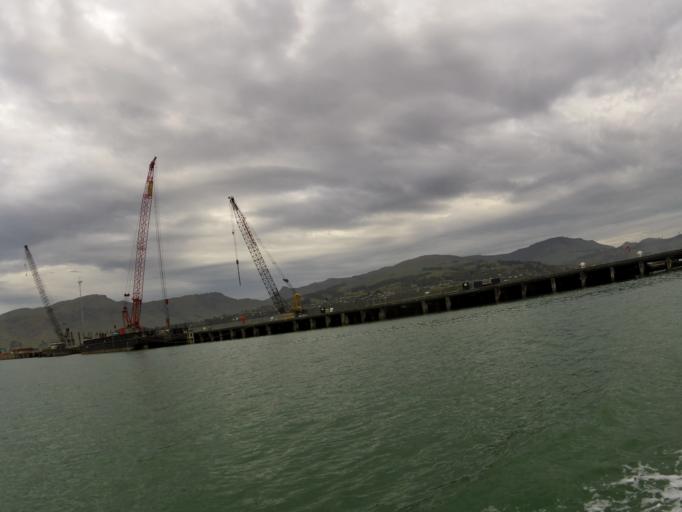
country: NZ
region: Canterbury
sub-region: Christchurch City
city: Christchurch
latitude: -43.6087
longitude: 172.7182
